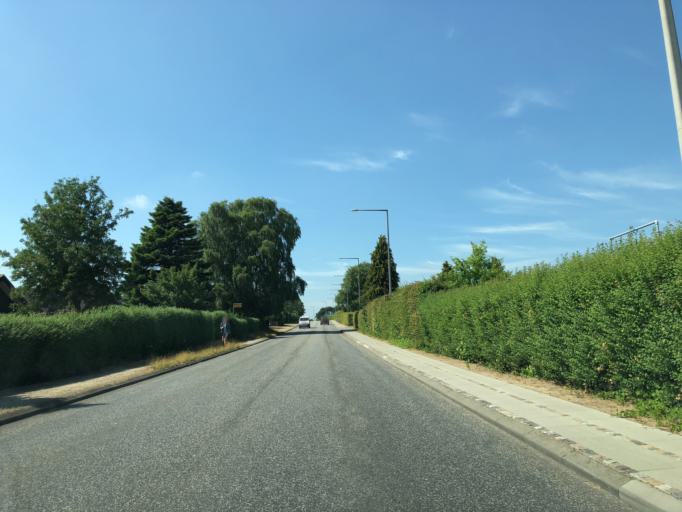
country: DK
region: South Denmark
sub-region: Kolding Kommune
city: Kolding
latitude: 55.5181
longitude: 9.4831
